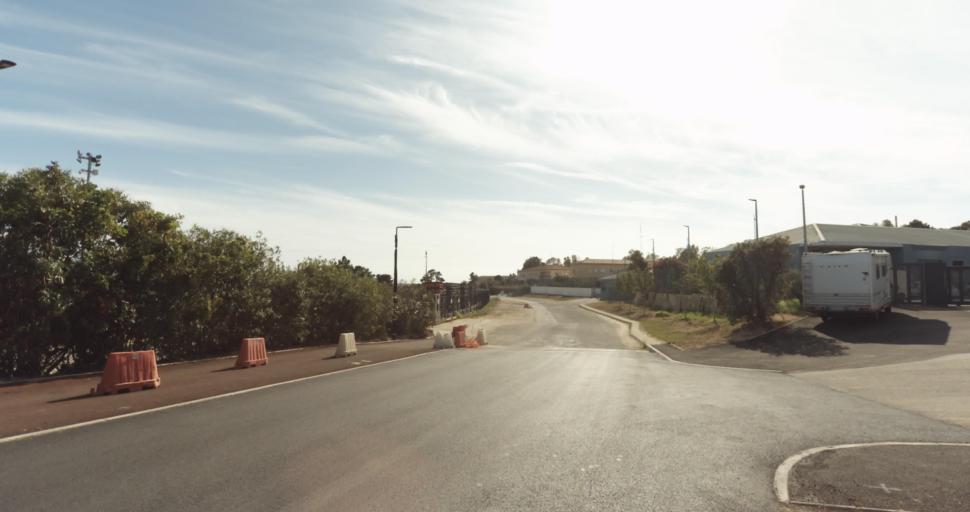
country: FR
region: Corsica
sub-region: Departement de la Corse-du-Sud
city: Ajaccio
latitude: 41.9282
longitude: 8.7681
